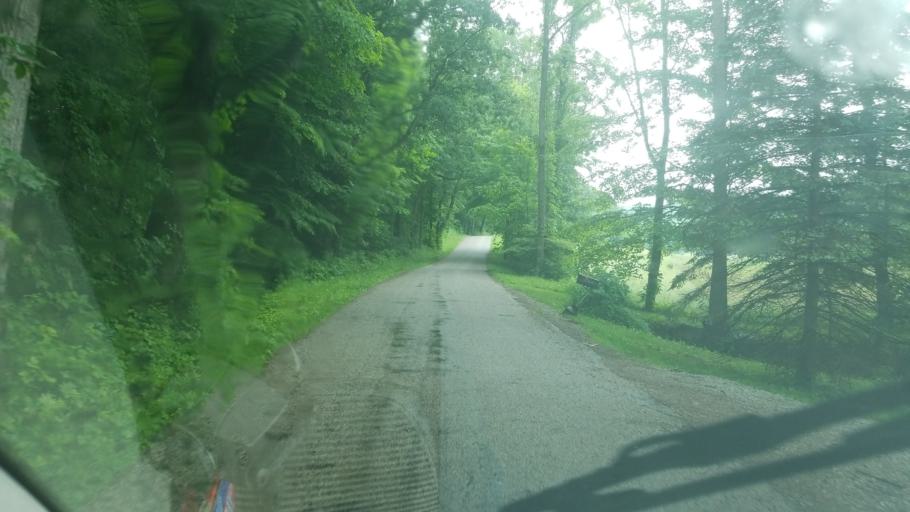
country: US
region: Ohio
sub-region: Sandusky County
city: Bellville
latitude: 40.6158
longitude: -82.4602
